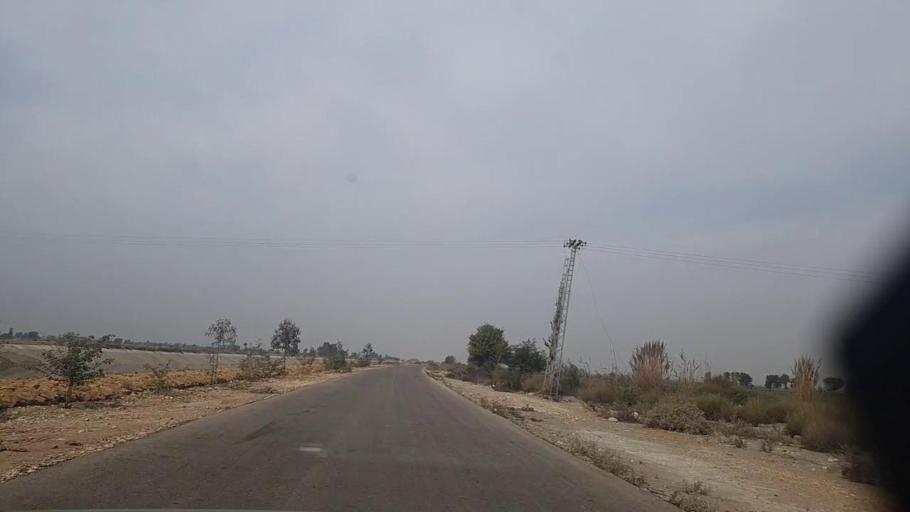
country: PK
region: Sindh
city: Sakrand
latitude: 26.2546
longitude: 68.2477
